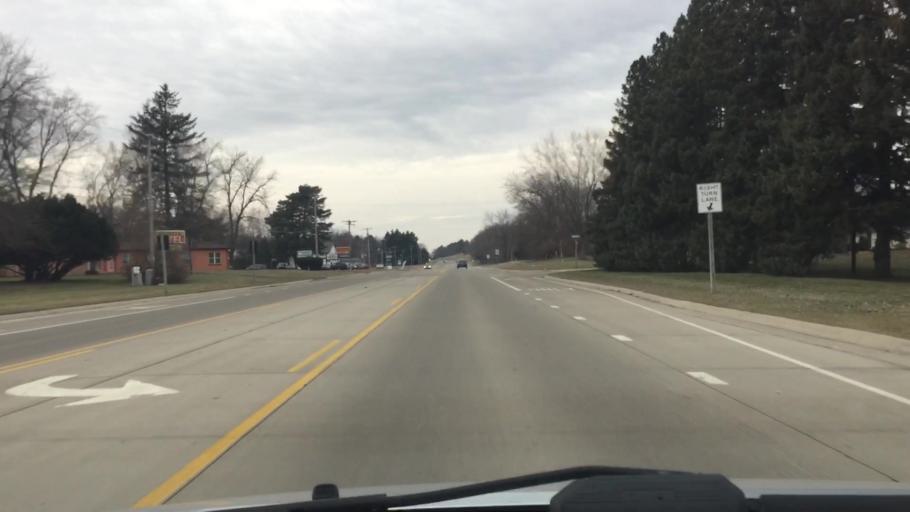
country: US
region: Wisconsin
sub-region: Waukesha County
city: Oconomowoc
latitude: 43.1264
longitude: -88.5337
